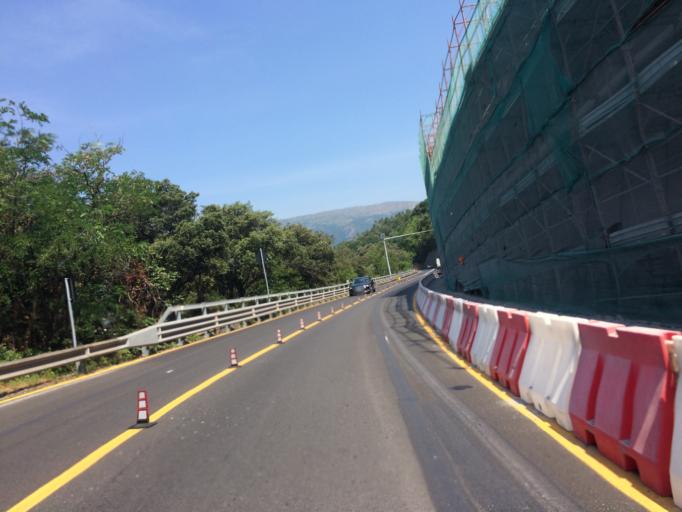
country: IT
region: Liguria
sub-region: Provincia di Genova
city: Cogoleto
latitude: 44.3927
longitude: 8.6652
